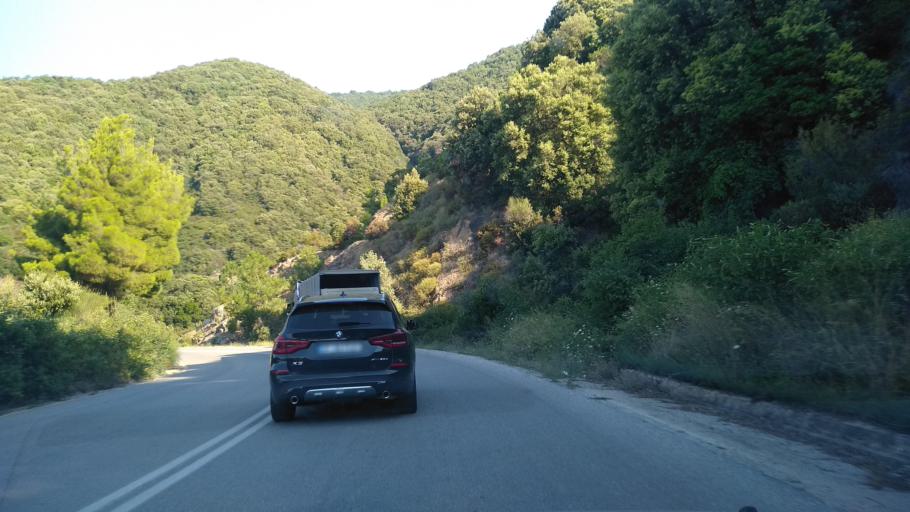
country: GR
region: Central Macedonia
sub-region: Nomos Chalkidikis
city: Stratonion
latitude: 40.5203
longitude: 23.8138
